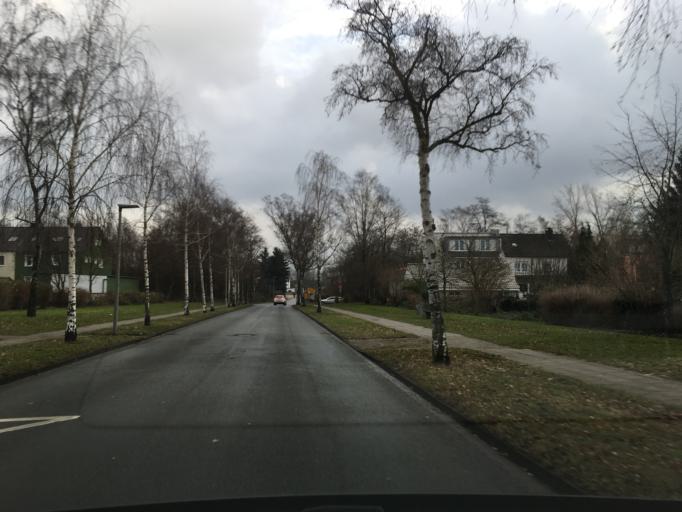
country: DE
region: North Rhine-Westphalia
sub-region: Regierungsbezirk Dusseldorf
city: Oberhausen
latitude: 51.4584
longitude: 6.8386
